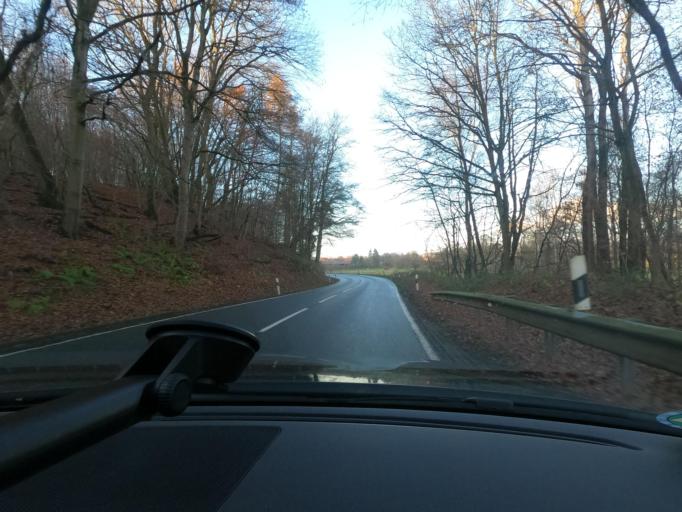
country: DE
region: Lower Saxony
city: Rhumspringe
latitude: 51.6064
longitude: 10.3274
